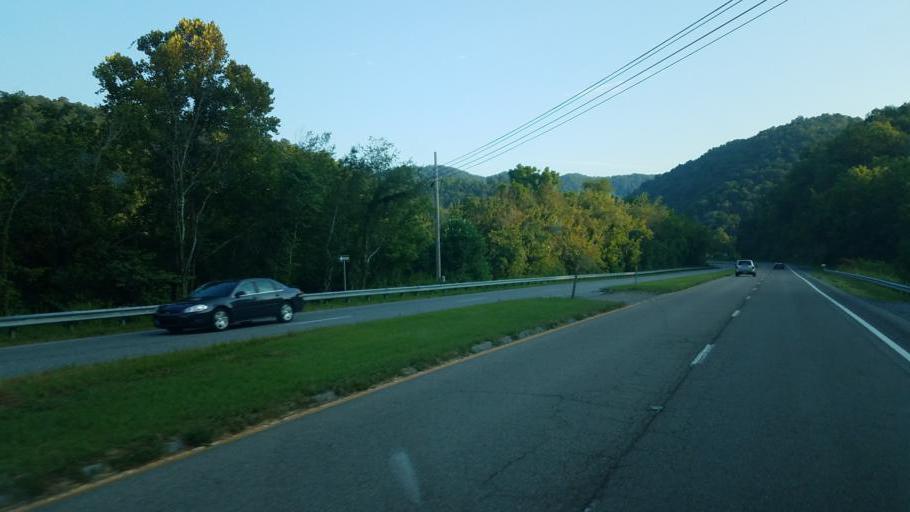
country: US
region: Tennessee
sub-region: Hawkins County
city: Church Hill
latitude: 36.6530
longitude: -82.7480
